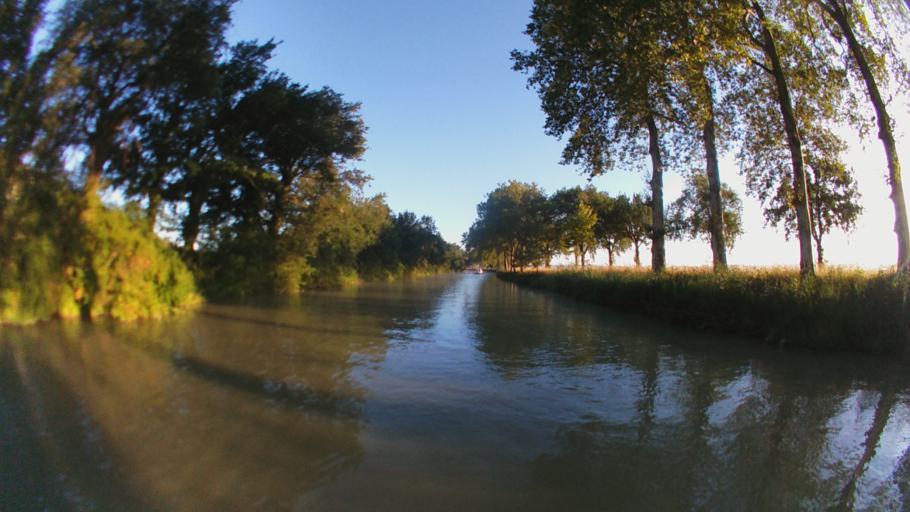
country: FR
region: Midi-Pyrenees
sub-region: Departement de la Haute-Garonne
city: Gardouch
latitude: 43.4054
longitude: 1.6661
